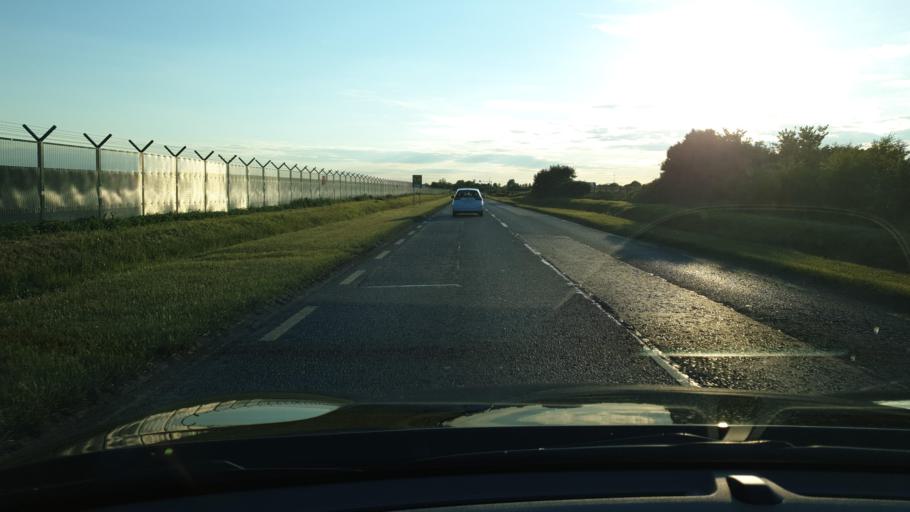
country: IE
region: Leinster
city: Ballymun
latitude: 53.4395
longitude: -6.2783
